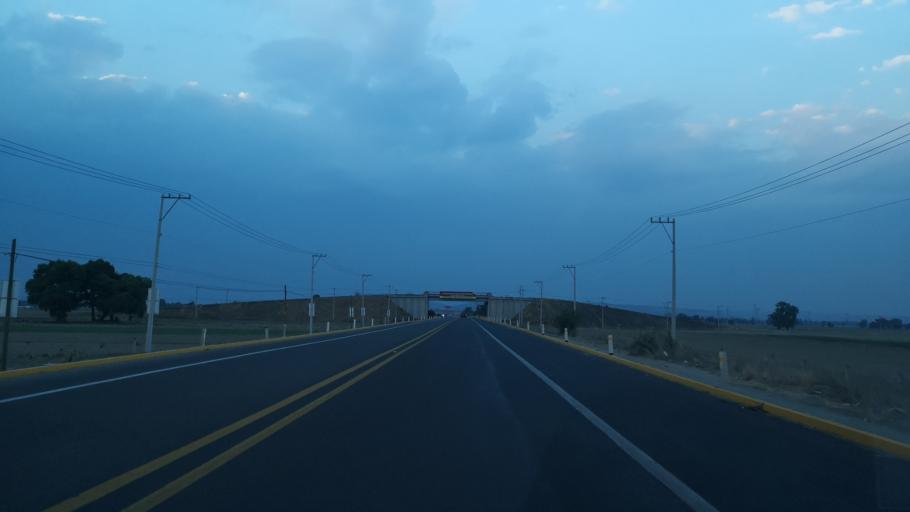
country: MX
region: Puebla
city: Santa Ana Xalmimilulco
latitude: 19.1850
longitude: -98.3703
